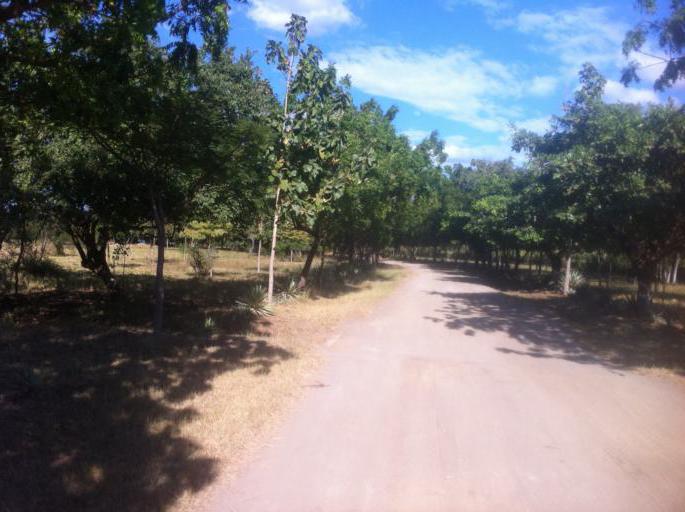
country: NI
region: Managua
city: Carlos Fonseca Amador
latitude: 11.9046
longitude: -86.6082
